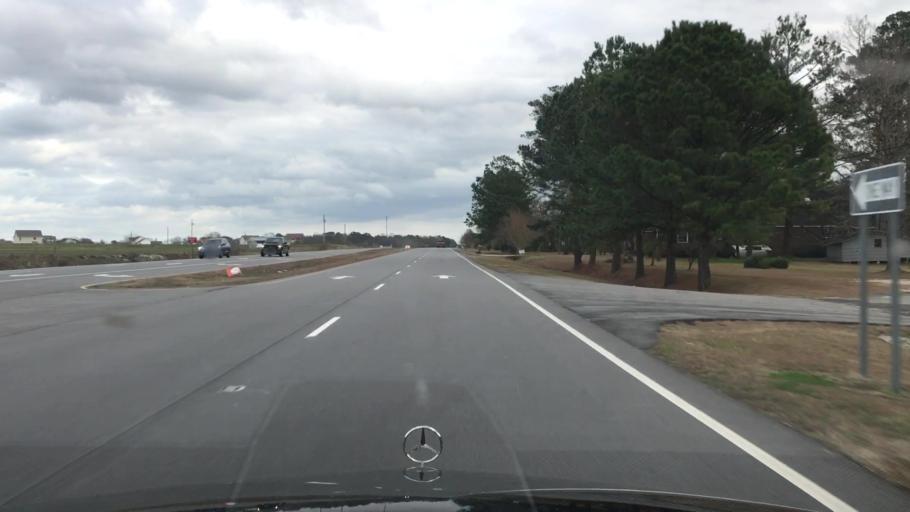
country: US
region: North Carolina
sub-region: Onslow County
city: Richlands
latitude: 34.9175
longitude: -77.6104
